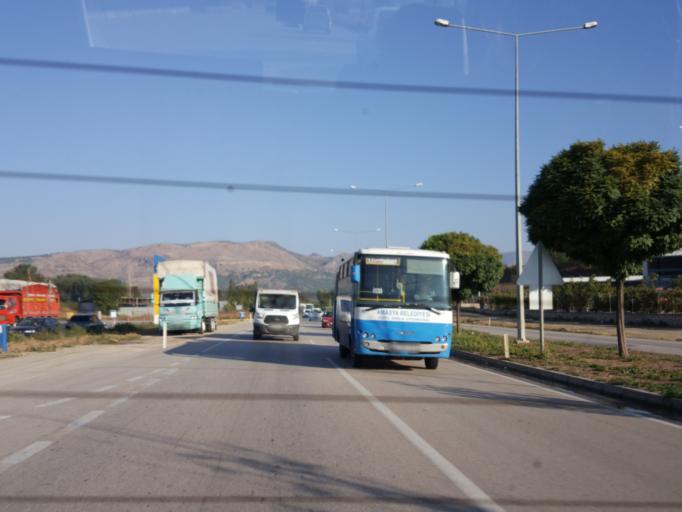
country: TR
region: Amasya
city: Amasya
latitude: 40.5656
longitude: 35.7883
